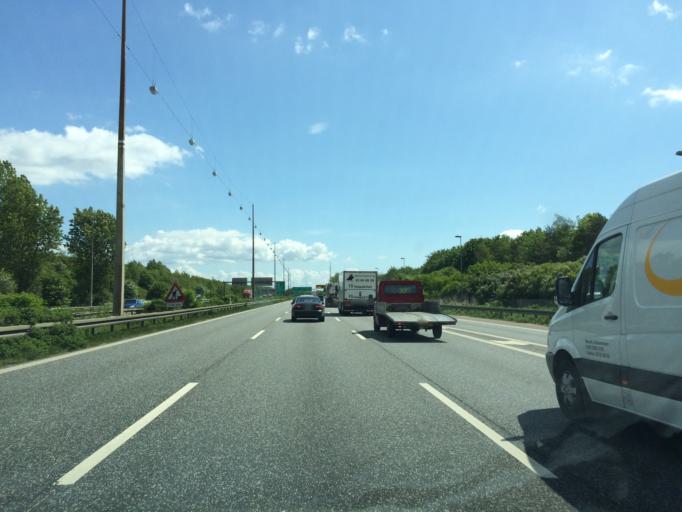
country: DK
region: Capital Region
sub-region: Brondby Kommune
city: Brondbyvester
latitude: 55.6414
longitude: 12.4023
